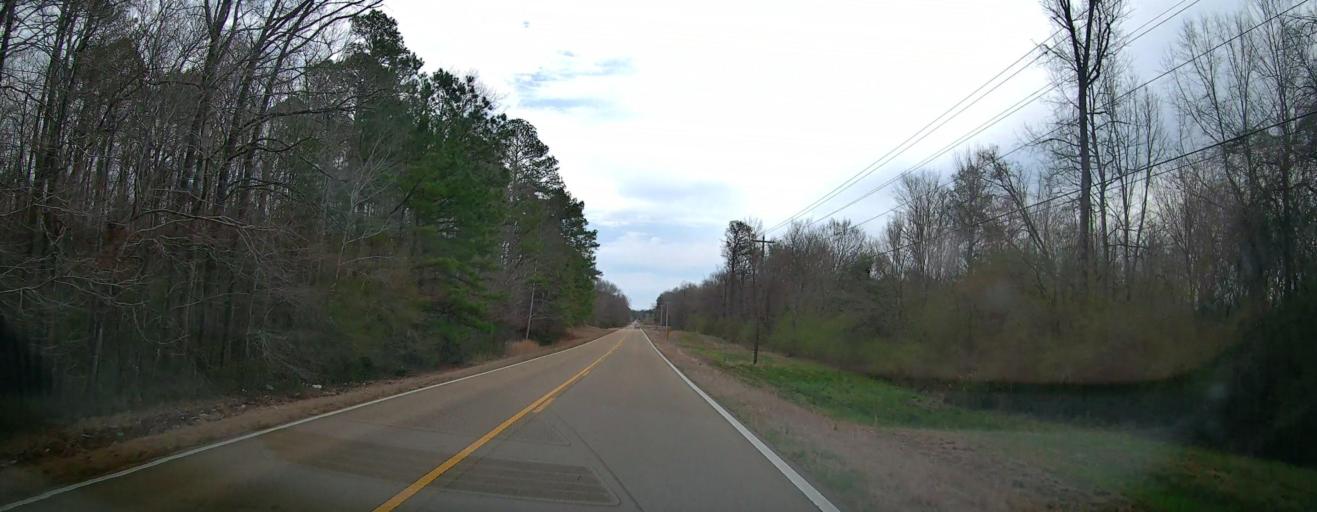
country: US
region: Mississippi
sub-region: Itawamba County
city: Fulton
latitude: 34.2591
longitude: -88.3196
